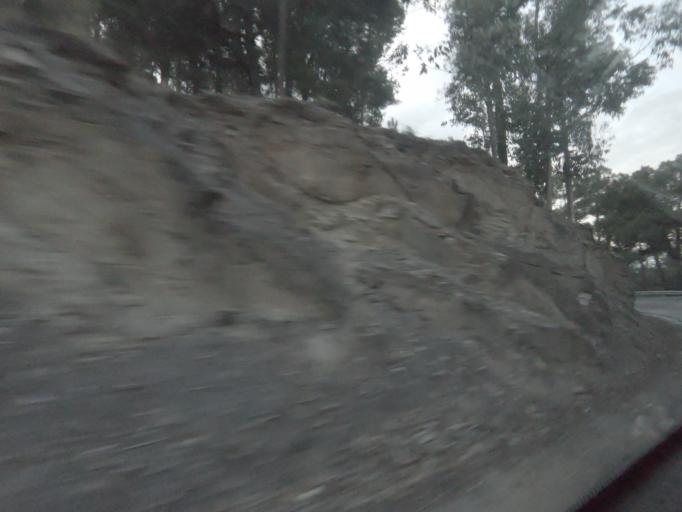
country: PT
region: Viseu
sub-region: Armamar
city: Armamar
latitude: 41.1252
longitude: -7.7315
